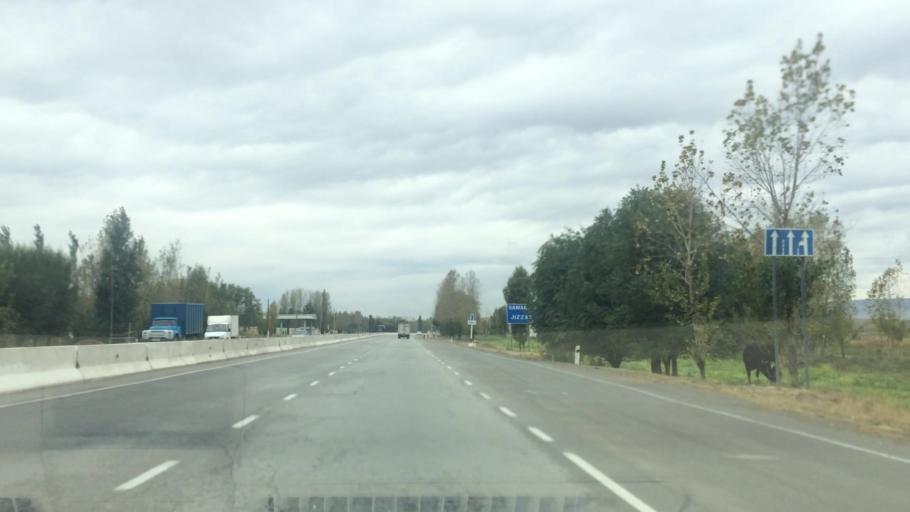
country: UZ
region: Jizzax
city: Jizzax
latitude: 39.9636
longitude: 67.5496
